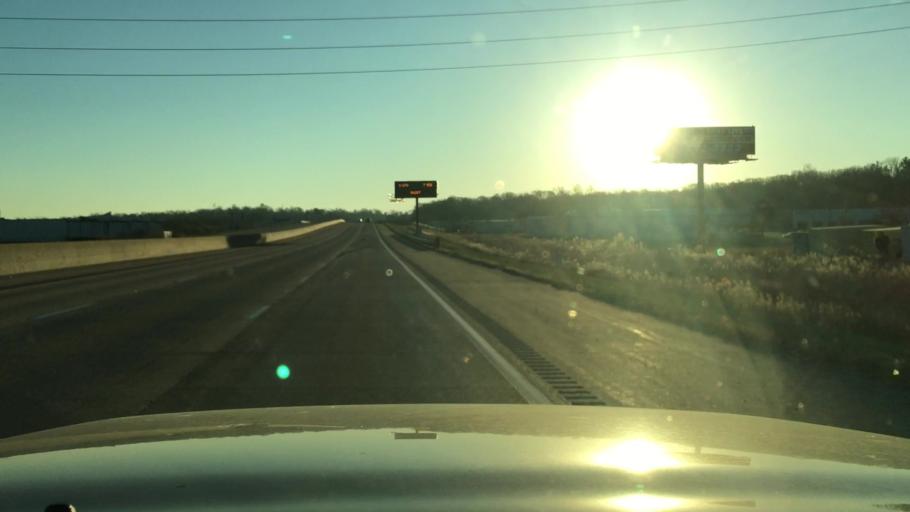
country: US
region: Missouri
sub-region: Saint Charles County
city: Saint Charles
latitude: 38.8224
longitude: -90.5112
